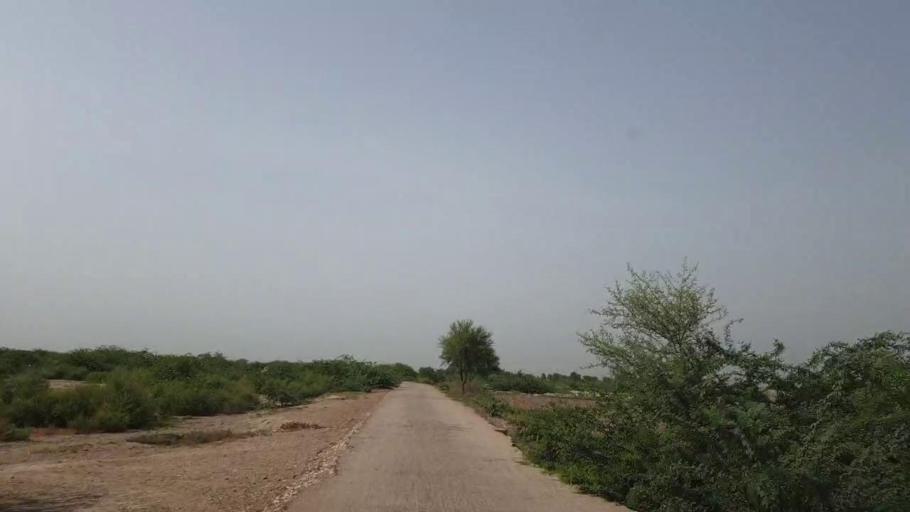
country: PK
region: Sindh
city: Nawabshah
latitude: 26.1119
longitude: 68.4398
